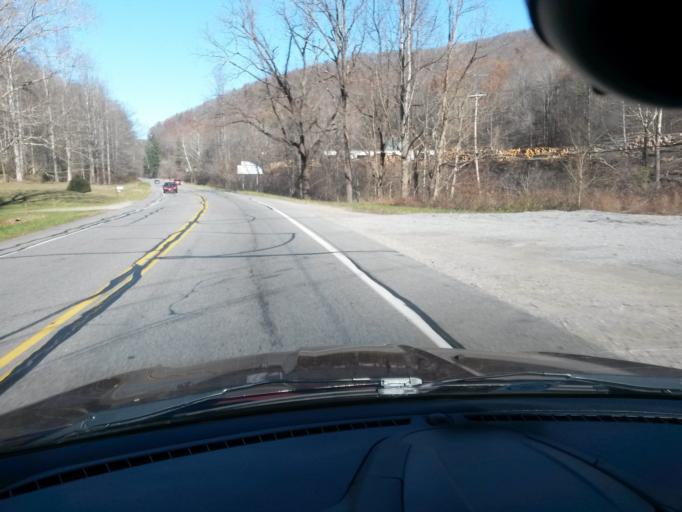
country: US
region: Virginia
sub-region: Patrick County
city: Stuart
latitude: 36.6676
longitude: -80.2737
